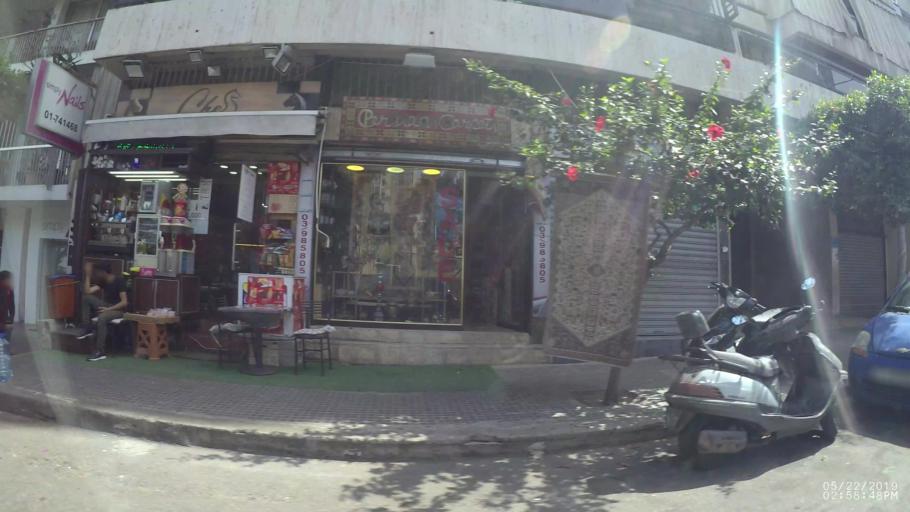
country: LB
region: Beyrouth
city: Ra's Bayrut
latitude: 33.8941
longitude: 35.4864
